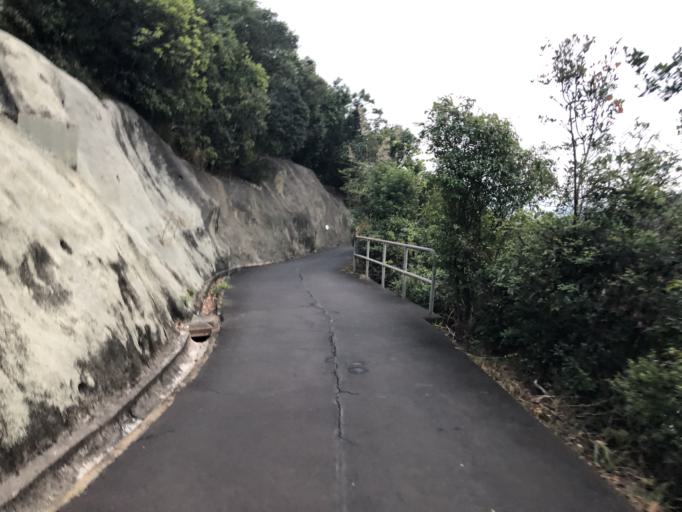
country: HK
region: Wanchai
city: Wan Chai
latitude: 22.2590
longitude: 114.2116
